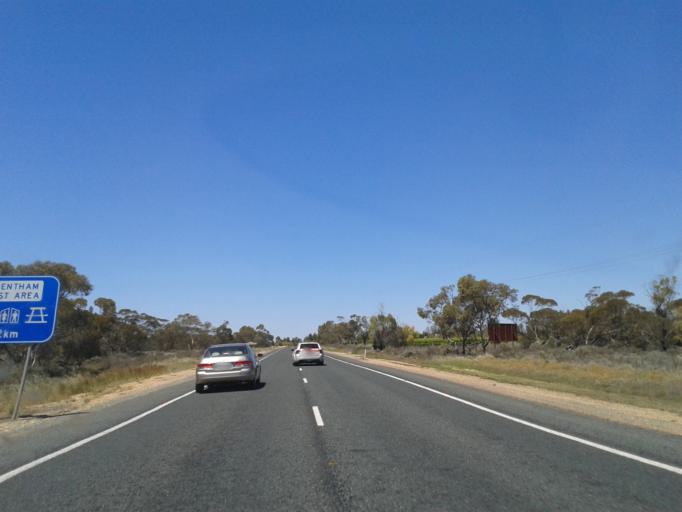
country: AU
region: New South Wales
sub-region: Wentworth
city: Gol Gol
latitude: -34.2023
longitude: 142.2447
